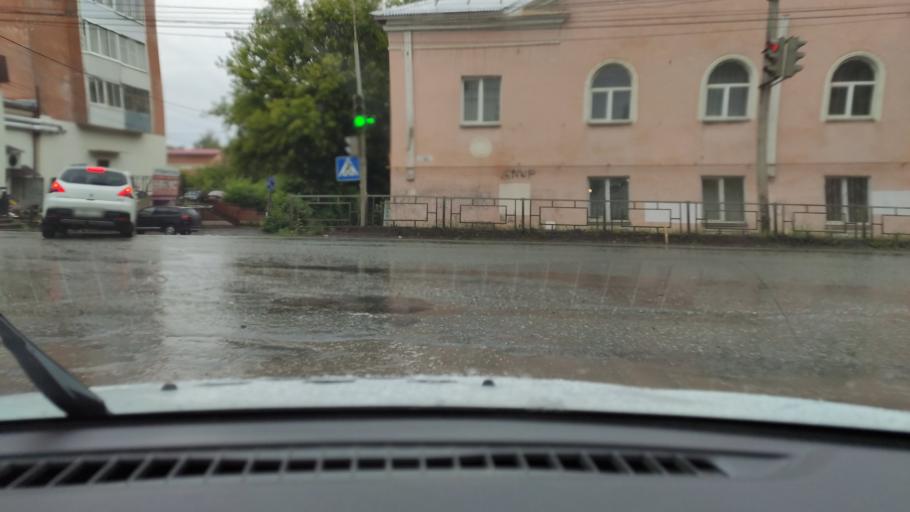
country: RU
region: Udmurtiya
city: Votkinsk
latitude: 57.0648
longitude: 53.9977
